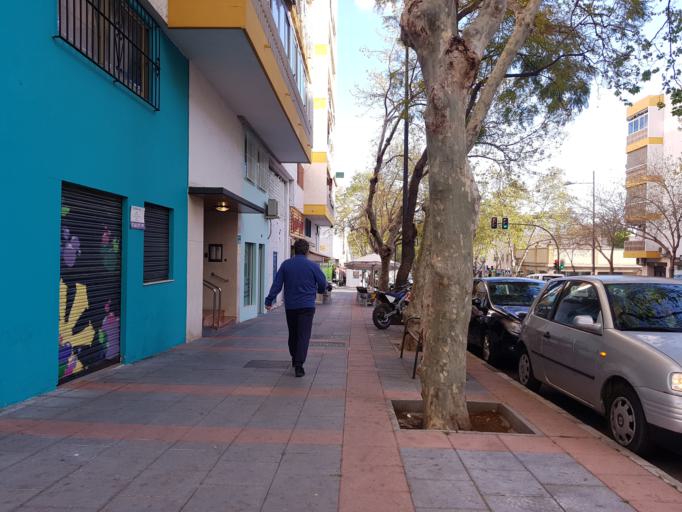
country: ES
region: Andalusia
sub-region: Provincia de Malaga
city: Marbella
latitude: 36.5146
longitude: -4.8770
